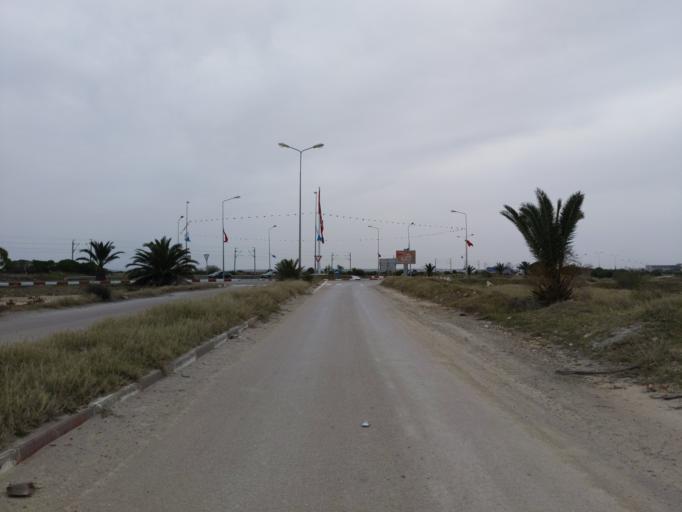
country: TN
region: Al Munastir
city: Saqanis
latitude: 35.7729
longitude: 10.7776
